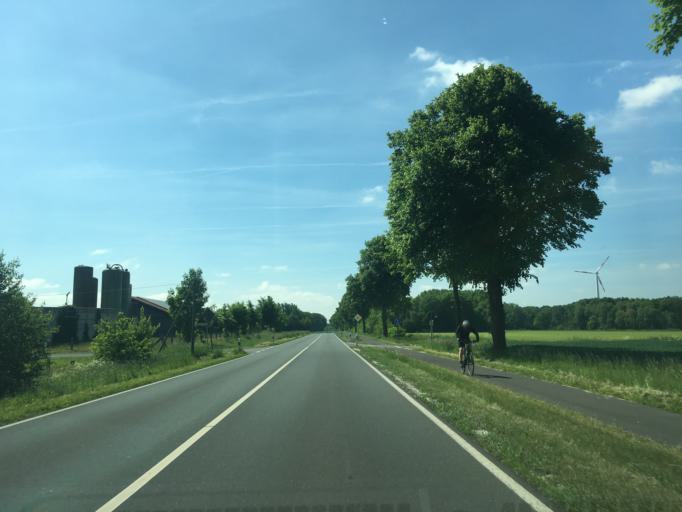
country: DE
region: North Rhine-Westphalia
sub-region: Regierungsbezirk Munster
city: Greven
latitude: 52.0620
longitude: 7.6133
